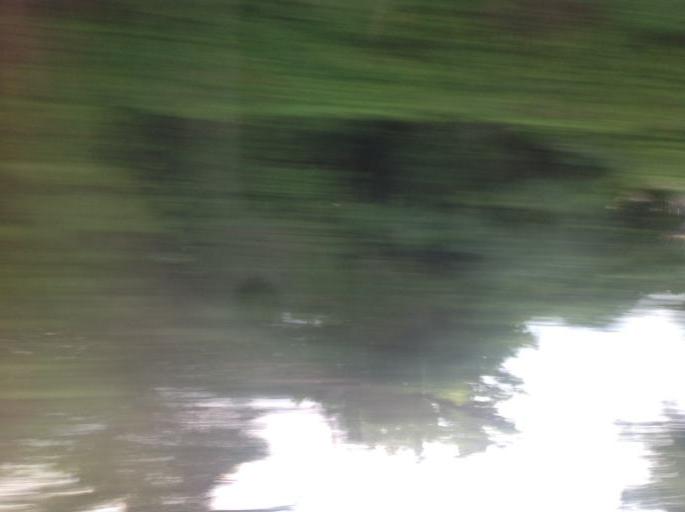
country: US
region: New York
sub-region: Montgomery County
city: Amsterdam
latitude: 42.9486
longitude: -74.2112
